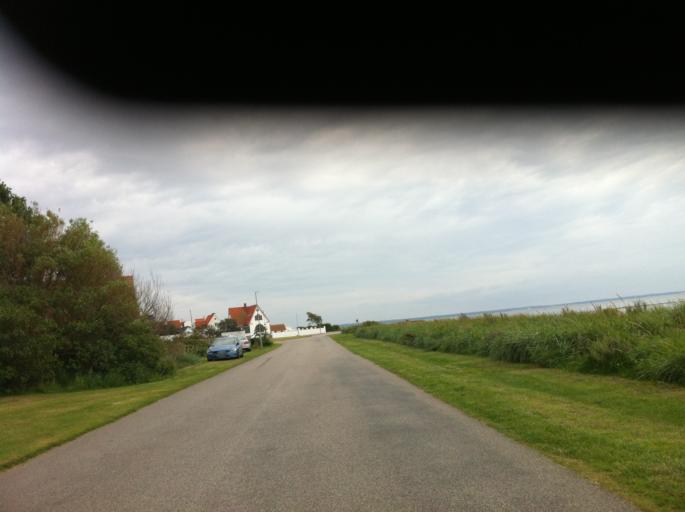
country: SE
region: Skane
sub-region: Hoganas Kommun
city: Hoganas
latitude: 56.2050
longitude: 12.5385
